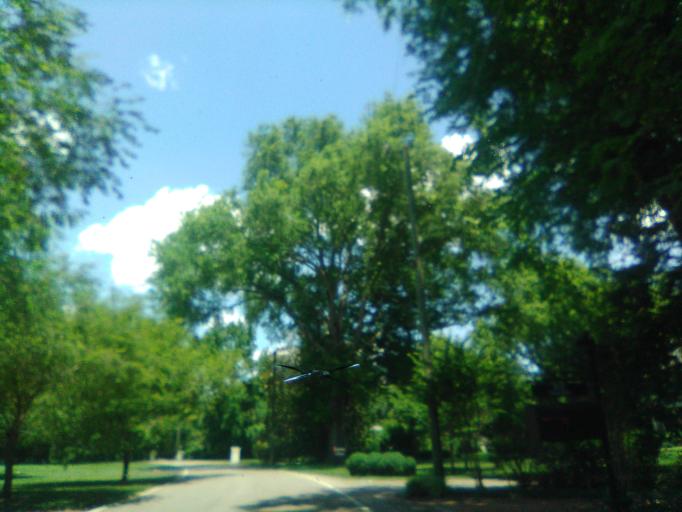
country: US
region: Tennessee
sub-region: Davidson County
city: Belle Meade
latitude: 36.1102
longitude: -86.8515
